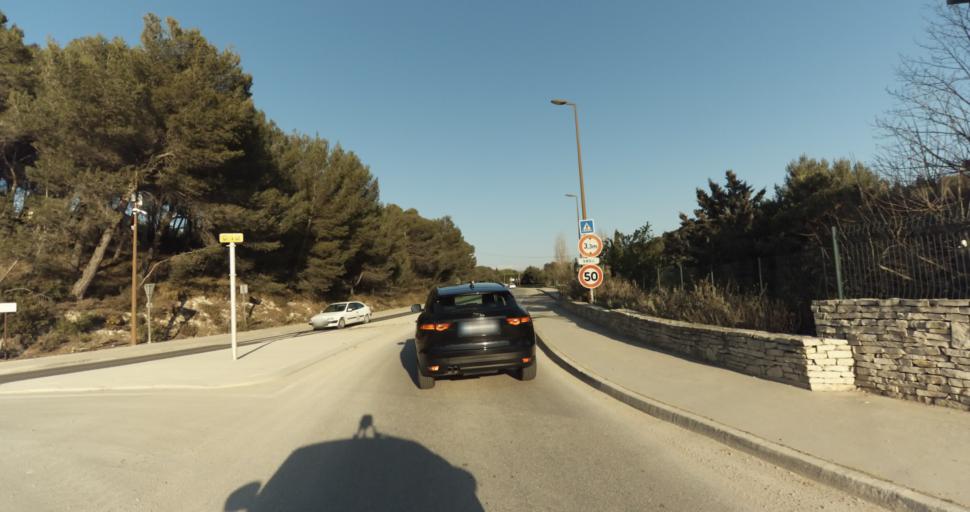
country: FR
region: Provence-Alpes-Cote d'Azur
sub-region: Departement des Bouches-du-Rhone
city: Ventabren
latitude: 43.5472
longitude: 5.3107
